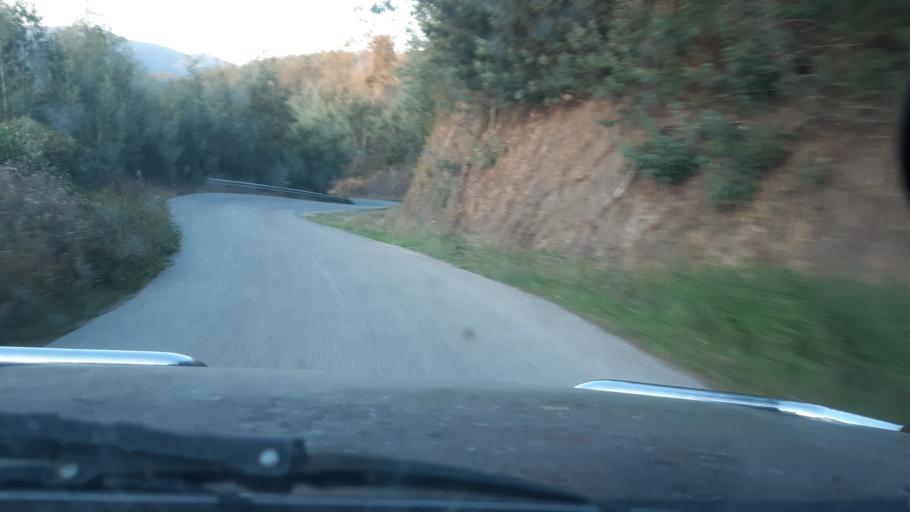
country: PT
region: Aveiro
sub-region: Agueda
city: Aguada de Cima
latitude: 40.5666
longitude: -8.3559
